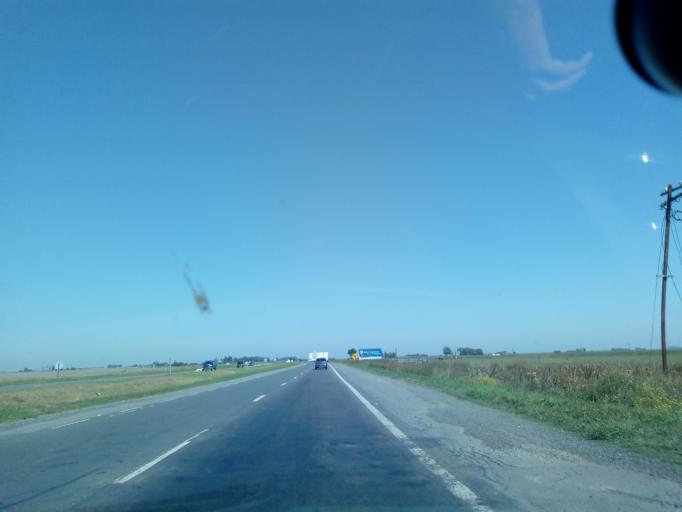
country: AR
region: Buenos Aires
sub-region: Partido de General Guido
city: General Guido
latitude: -36.6649
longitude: -57.7894
